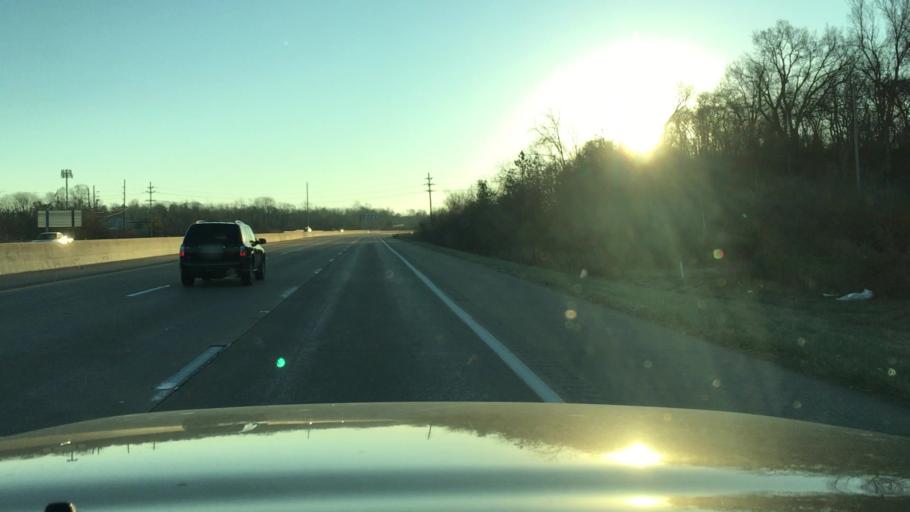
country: US
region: Missouri
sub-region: Saint Charles County
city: Saint Charles
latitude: 38.8196
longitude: -90.5019
